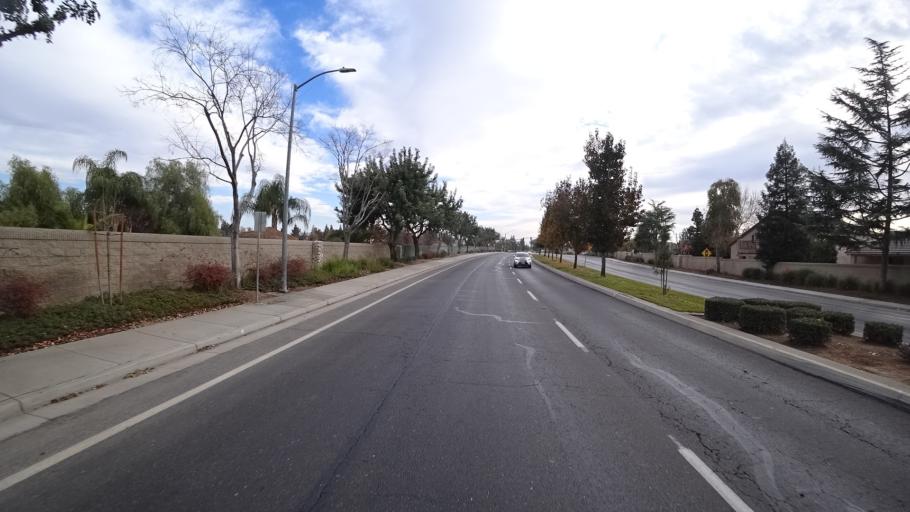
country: US
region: California
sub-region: Kern County
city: Greenacres
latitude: 35.4139
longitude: -119.1032
